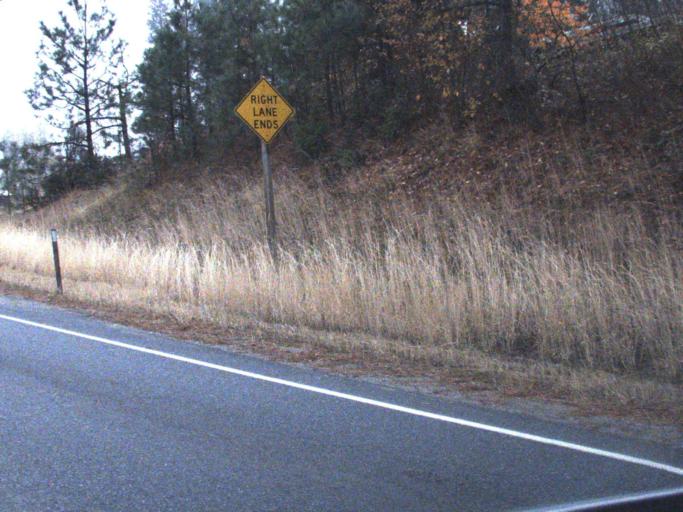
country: US
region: Washington
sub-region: Stevens County
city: Kettle Falls
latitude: 48.6124
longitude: -118.0958
